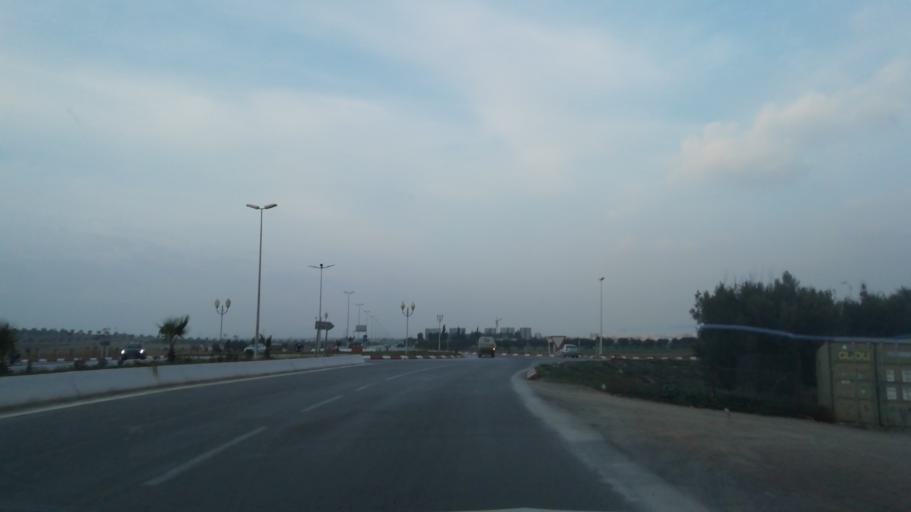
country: DZ
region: Sidi Bel Abbes
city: Sidi Bel Abbes
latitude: 35.1946
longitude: -0.6615
